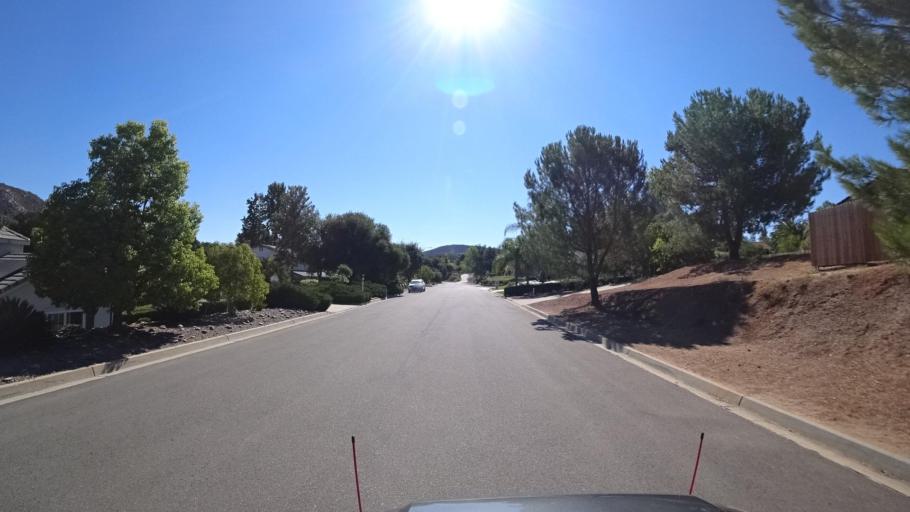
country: US
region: California
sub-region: San Diego County
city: San Diego Country Estates
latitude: 33.0023
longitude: -116.7759
